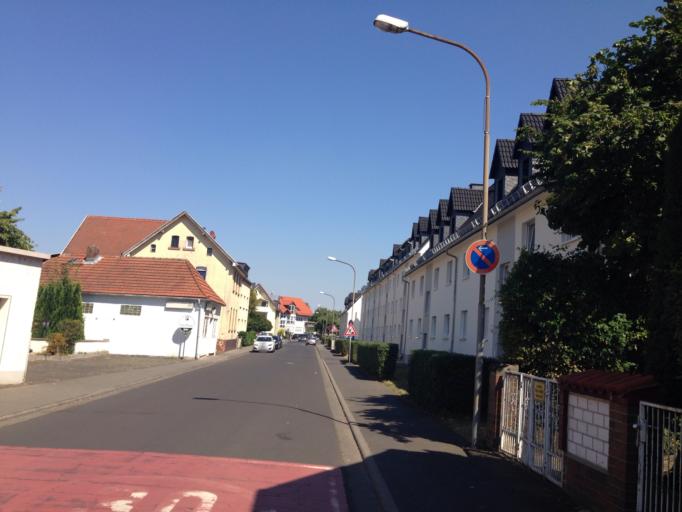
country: DE
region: Hesse
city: Lollar
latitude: 50.6449
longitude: 8.7040
